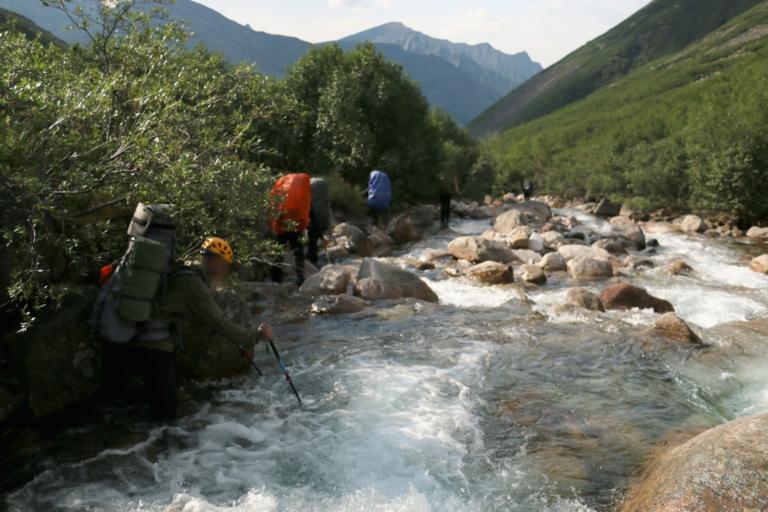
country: RU
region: Respublika Buryatiya
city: Novyy Uoyan
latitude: 56.3235
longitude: 111.1992
